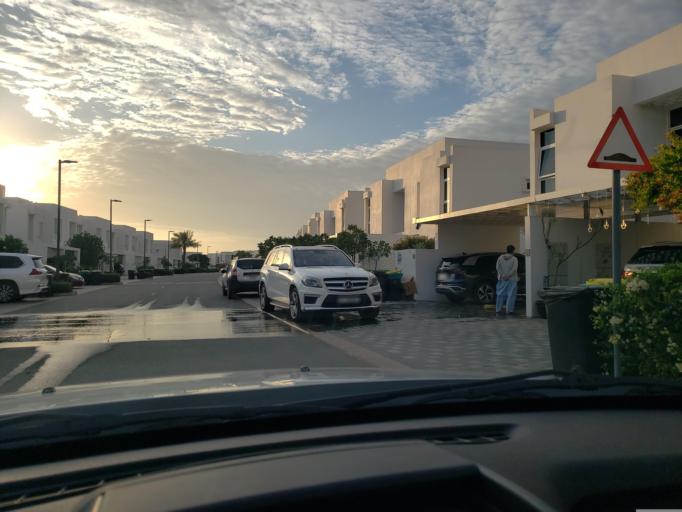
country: AE
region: Dubai
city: Dubai
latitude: 25.0186
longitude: 55.2724
